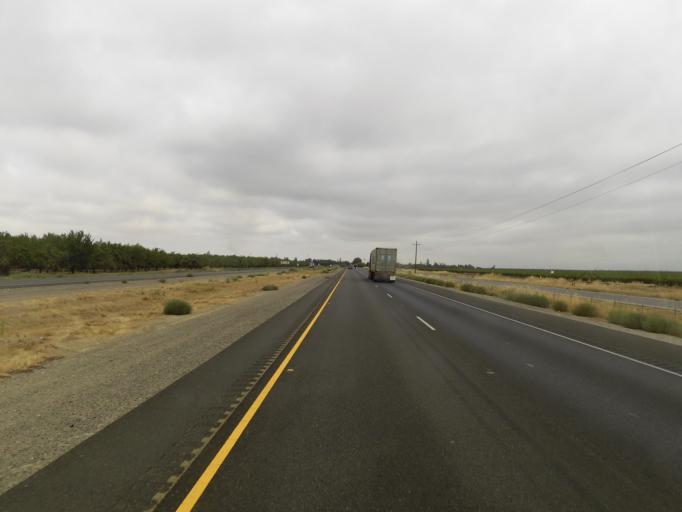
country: US
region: California
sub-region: Colusa County
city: Arbuckle
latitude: 39.0016
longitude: -122.0467
